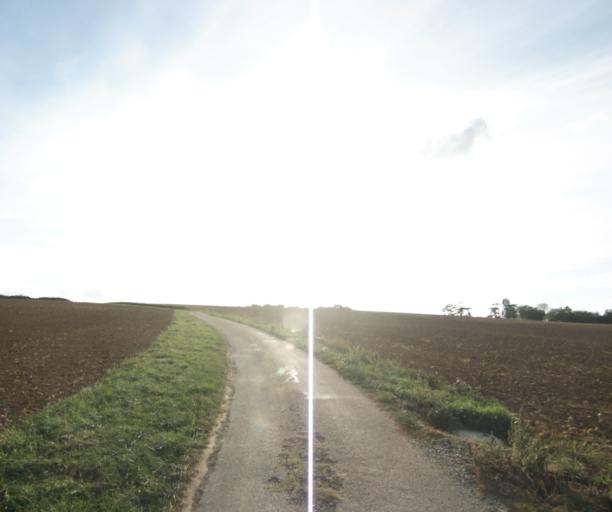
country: FR
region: Midi-Pyrenees
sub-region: Departement du Gers
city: Gondrin
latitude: 43.8967
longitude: 0.2694
